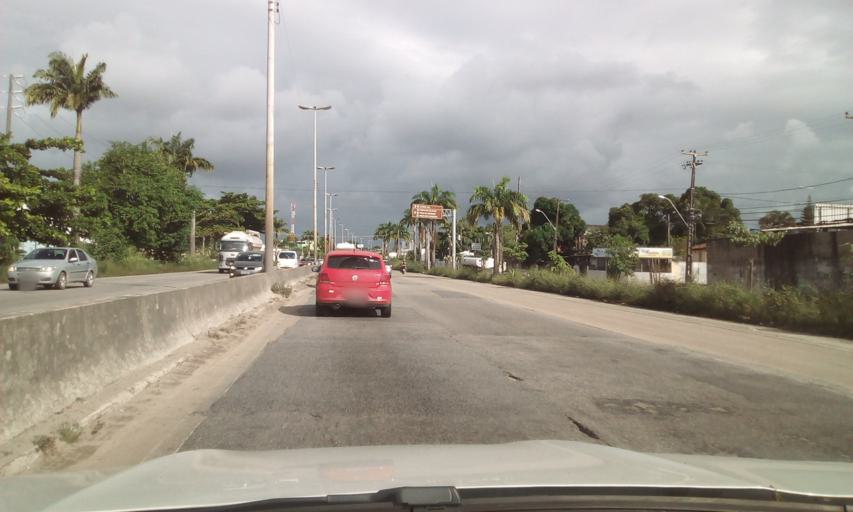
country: BR
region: Pernambuco
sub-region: Recife
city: Recife
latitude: -8.0314
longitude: -34.9427
